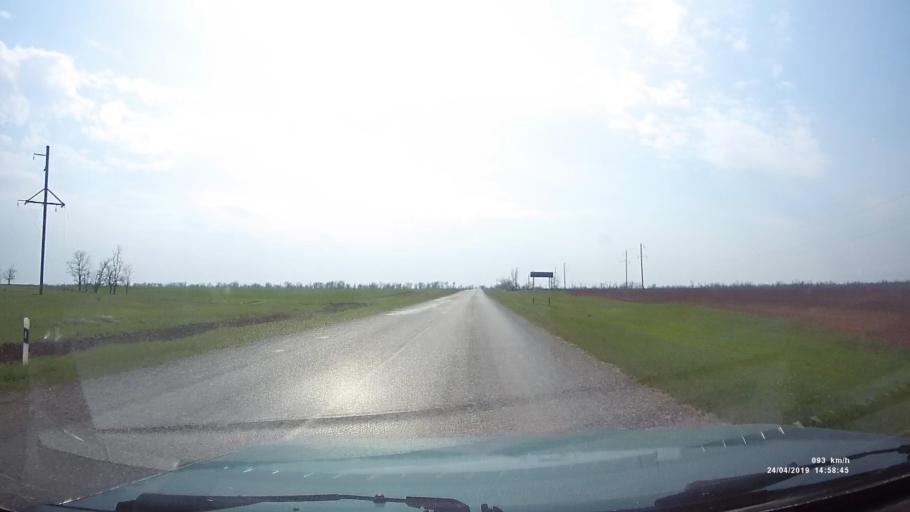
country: RU
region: Rostov
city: Remontnoye
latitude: 46.5679
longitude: 43.5917
